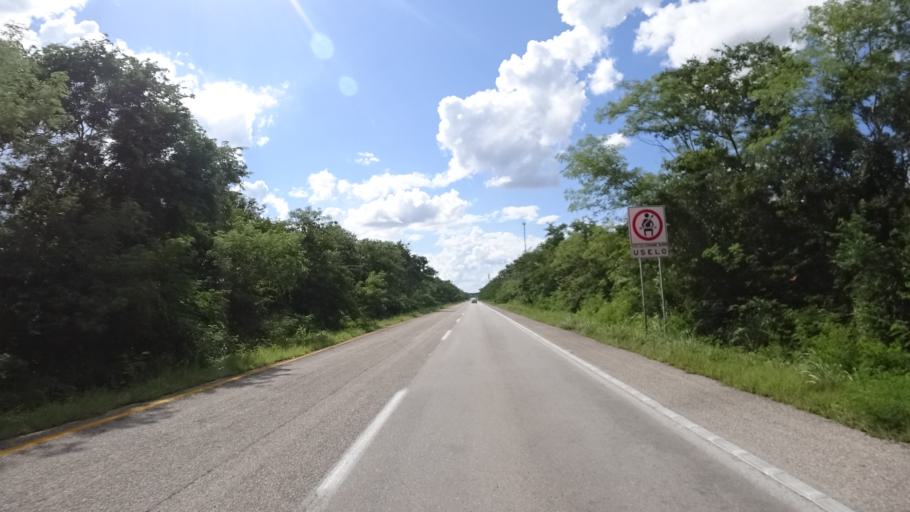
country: MX
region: Yucatan
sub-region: Kantunil
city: Kantunil
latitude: 20.8037
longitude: -89.0152
